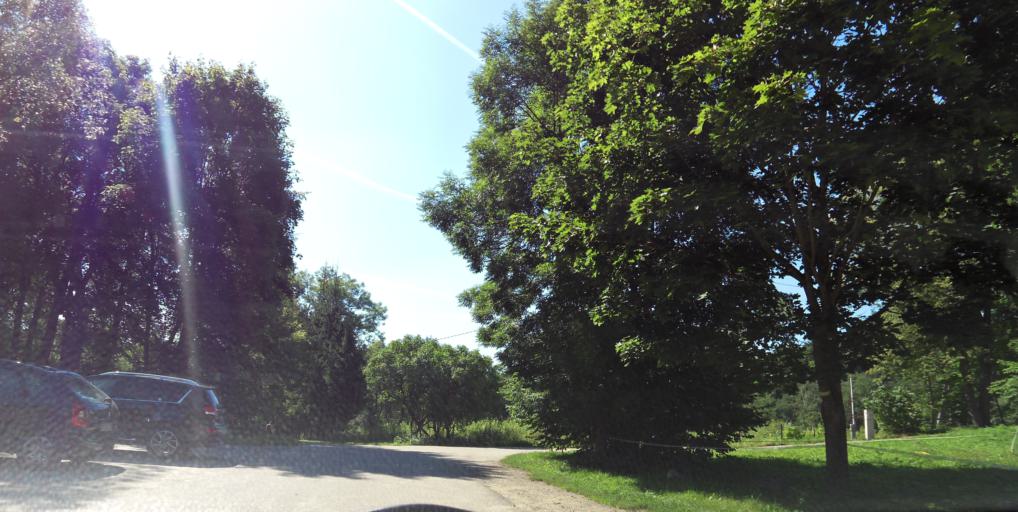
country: LT
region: Vilnius County
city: Rasos
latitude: 54.6867
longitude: 25.3574
